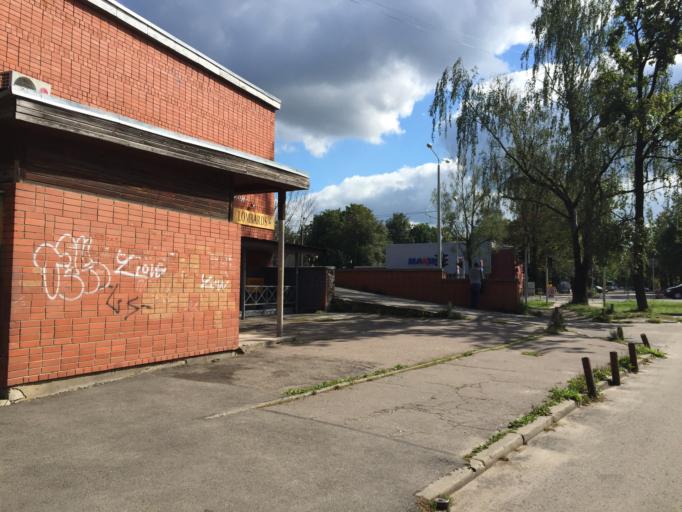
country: LV
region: Riga
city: Bergi
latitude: 56.9895
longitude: 24.2370
